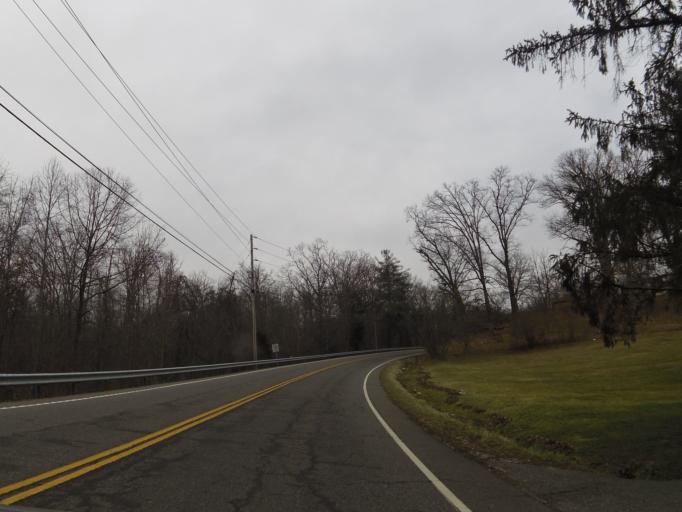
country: US
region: Tennessee
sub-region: Morgan County
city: Wartburg
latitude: 36.2561
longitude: -84.6665
